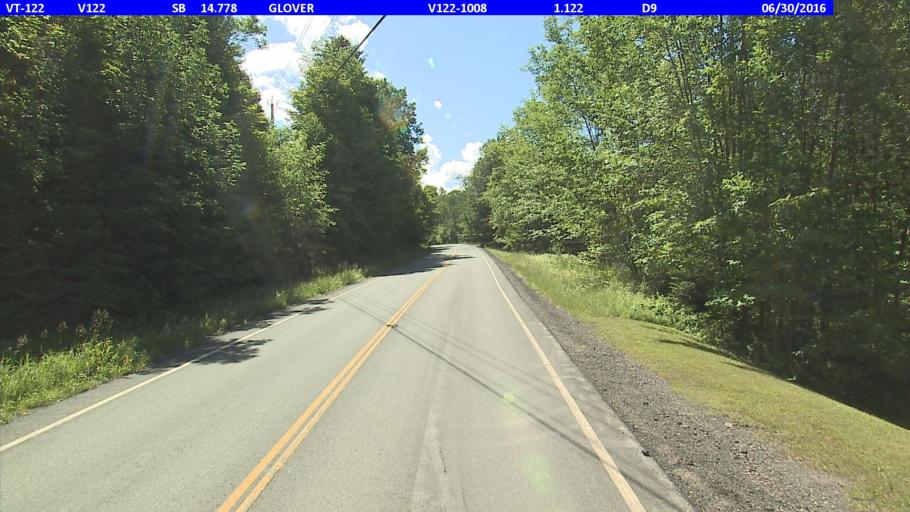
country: US
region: Vermont
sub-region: Caledonia County
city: Lyndonville
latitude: 44.6866
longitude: -72.1833
